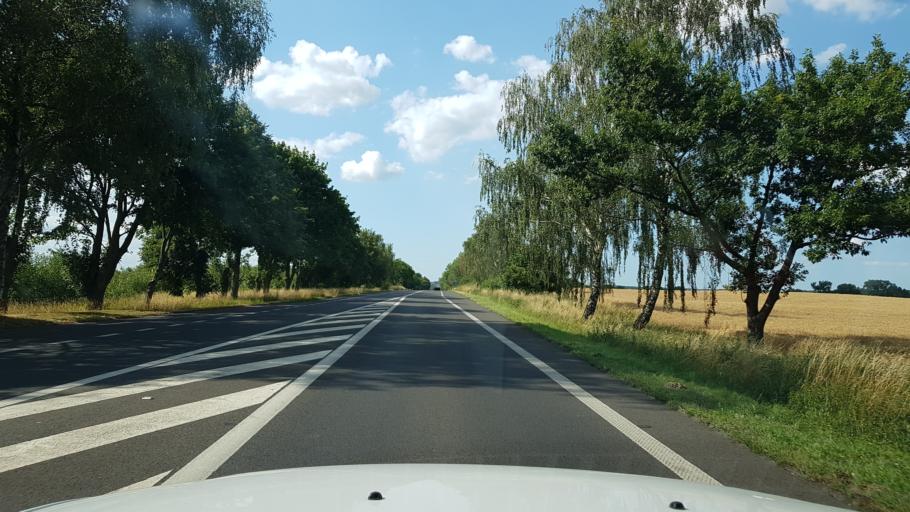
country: PL
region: West Pomeranian Voivodeship
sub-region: Powiat gryfinski
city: Stare Czarnowo
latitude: 53.2314
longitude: 14.7915
